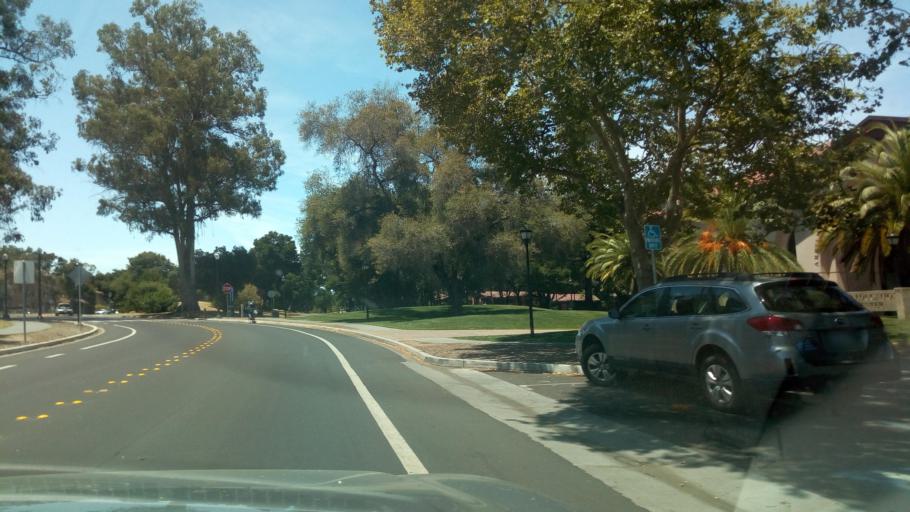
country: US
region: California
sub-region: Santa Clara County
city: Stanford
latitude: 37.4263
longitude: -122.1774
